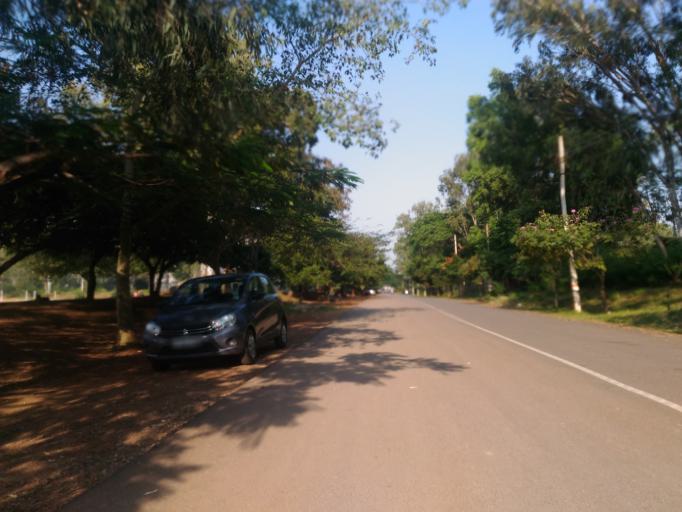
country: IN
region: Karnataka
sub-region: Bangalore Urban
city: Bangalore
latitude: 12.9385
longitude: 77.5004
